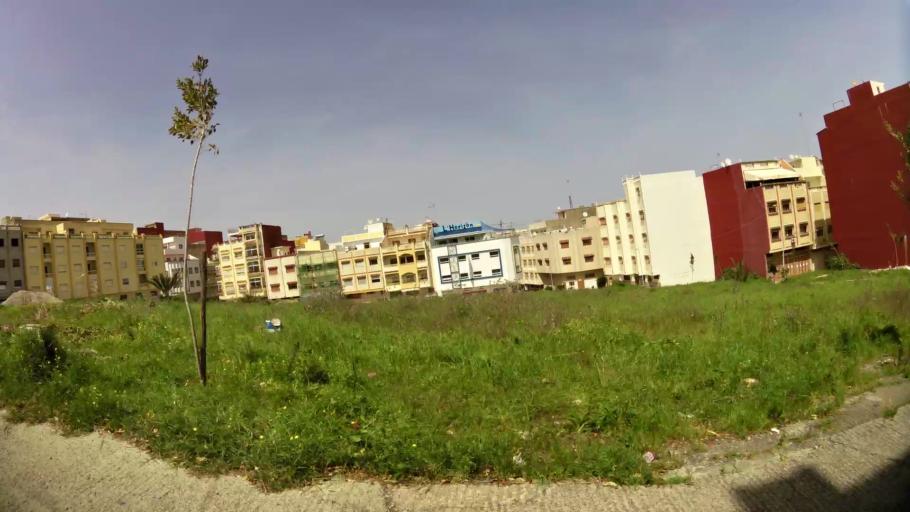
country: MA
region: Tanger-Tetouan
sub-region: Tanger-Assilah
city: Tangier
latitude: 35.7592
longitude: -5.8369
